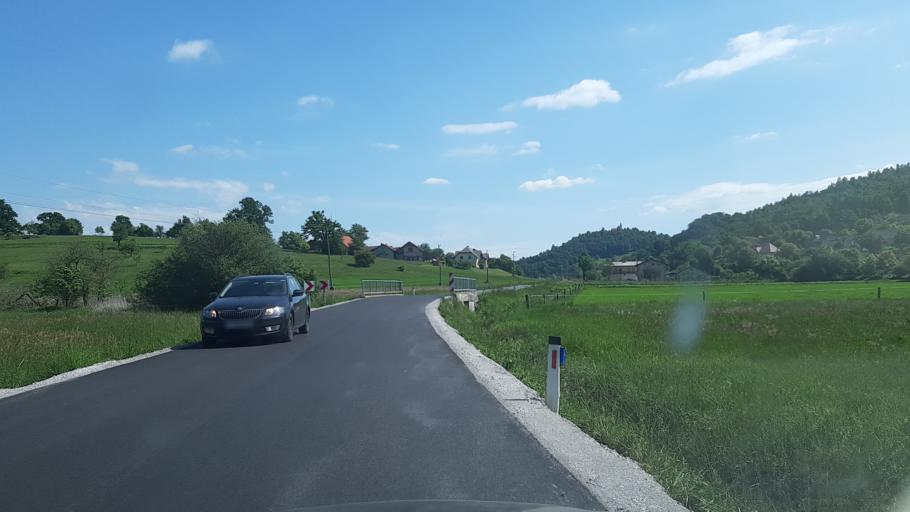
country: SI
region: Borovnica
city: Borovnica
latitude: 45.9493
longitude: 14.3756
